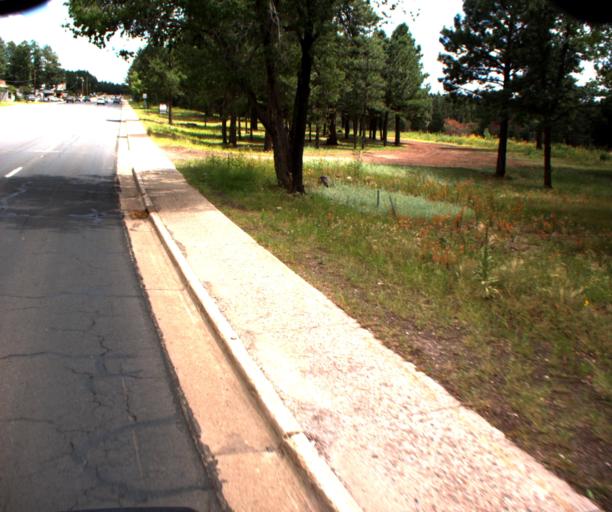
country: US
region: Arizona
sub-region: Navajo County
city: Pinetop-Lakeside
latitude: 34.1256
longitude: -109.9306
